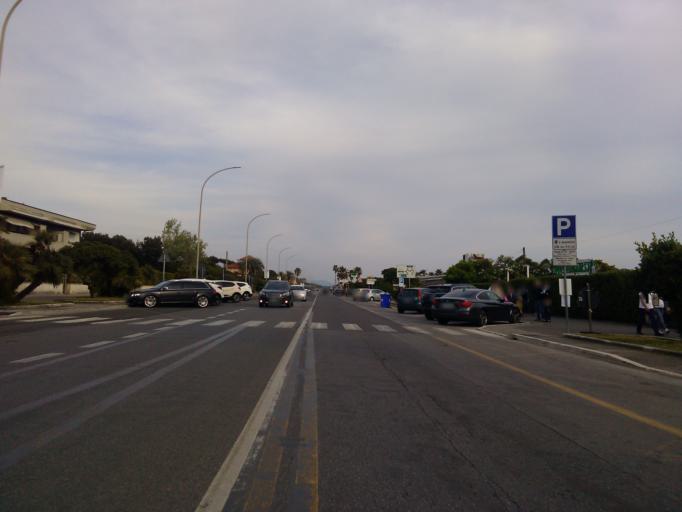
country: IT
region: Tuscany
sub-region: Provincia di Massa-Carrara
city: Massa
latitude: 44.0039
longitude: 10.1054
